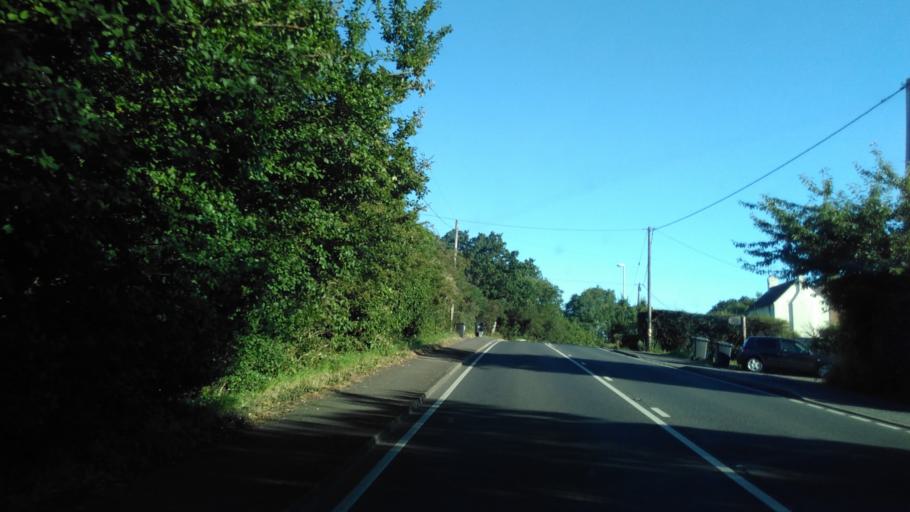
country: GB
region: England
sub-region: Kent
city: Blean
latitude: 51.3225
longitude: 1.0275
